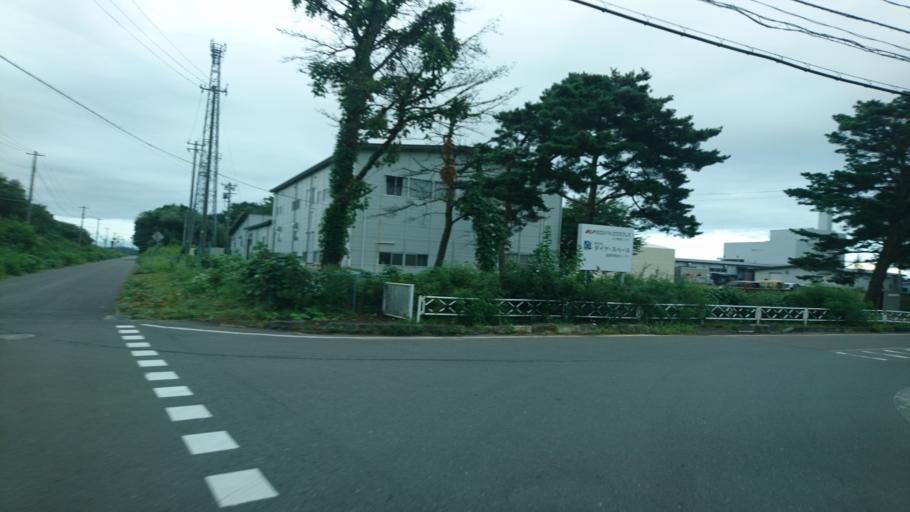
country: JP
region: Iwate
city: Kitakami
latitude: 39.3298
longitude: 141.0117
